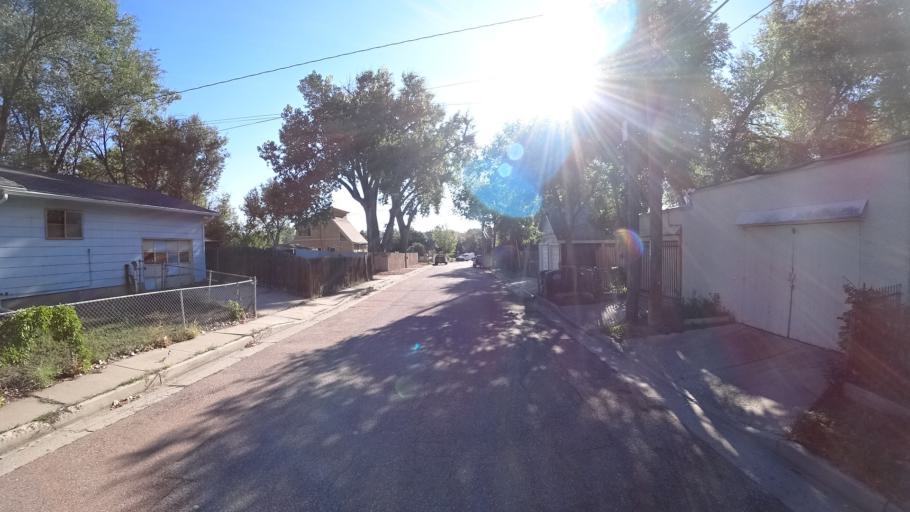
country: US
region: Colorado
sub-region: El Paso County
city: Colorado Springs
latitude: 38.8390
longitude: -104.8321
